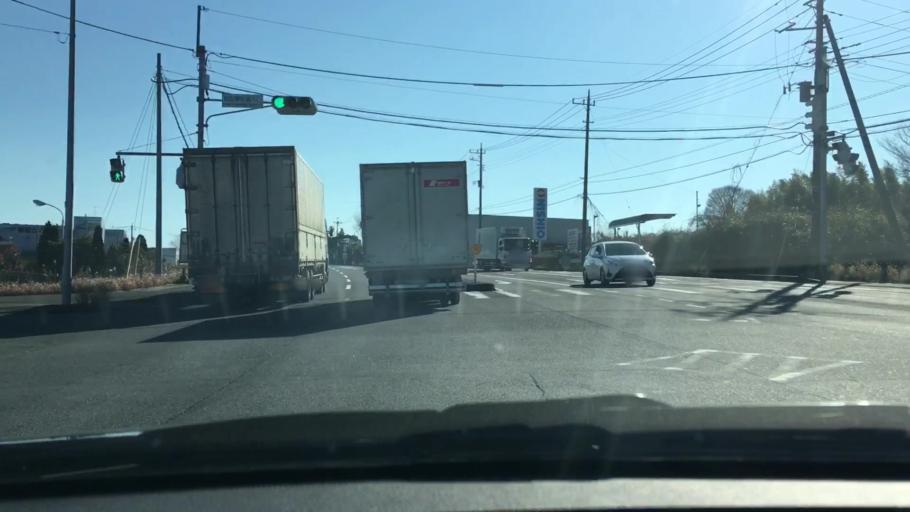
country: JP
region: Chiba
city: Narita
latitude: 35.7370
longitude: 140.4003
